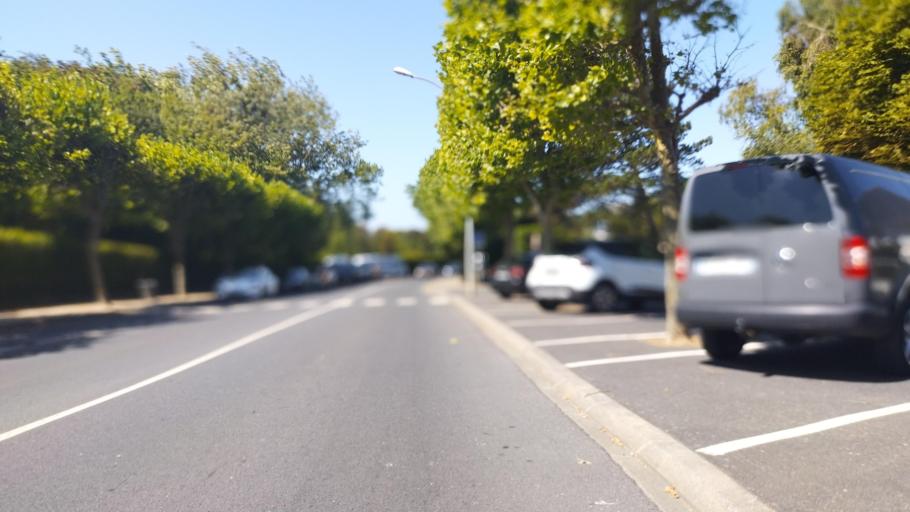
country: FR
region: Lower Normandy
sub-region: Departement du Calvados
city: Courseulles-sur-Mer
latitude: 49.3305
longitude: -0.4599
